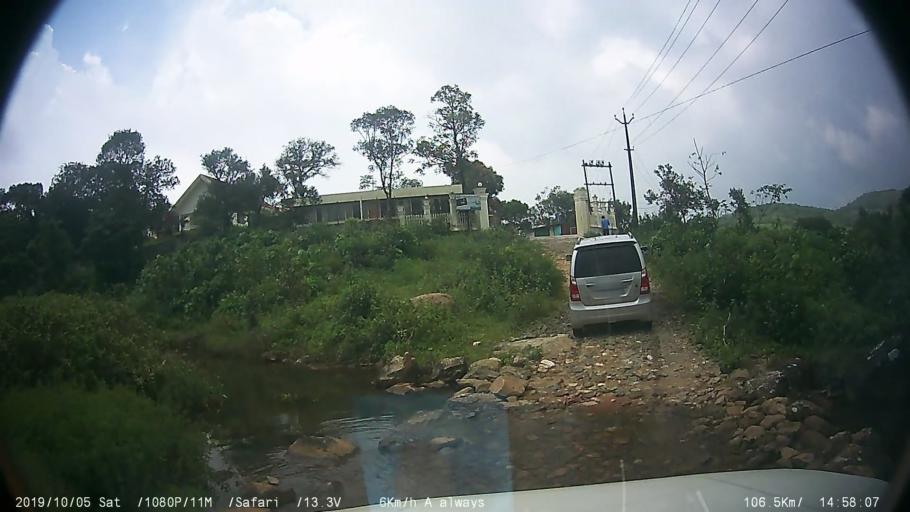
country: IN
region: Kerala
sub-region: Kottayam
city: Erattupetta
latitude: 9.6200
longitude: 76.9347
